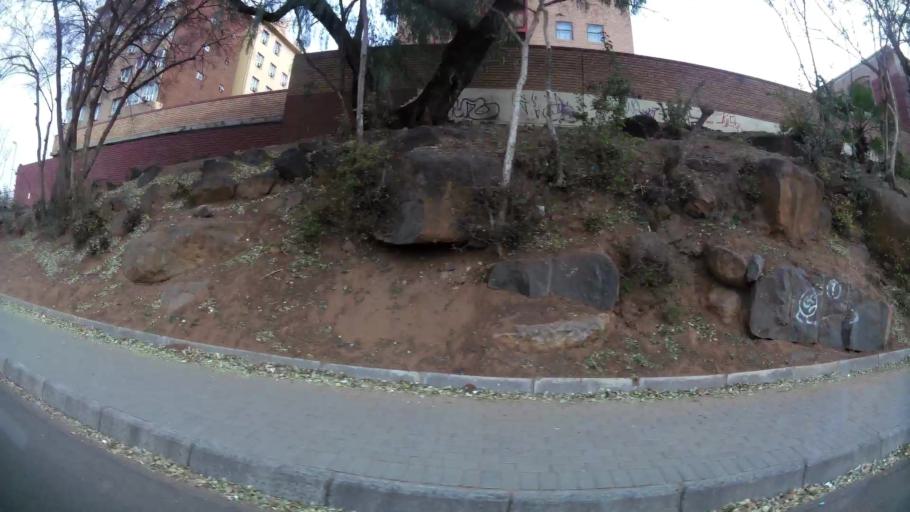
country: ZA
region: Orange Free State
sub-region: Mangaung Metropolitan Municipality
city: Bloemfontein
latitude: -29.1176
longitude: 26.2135
